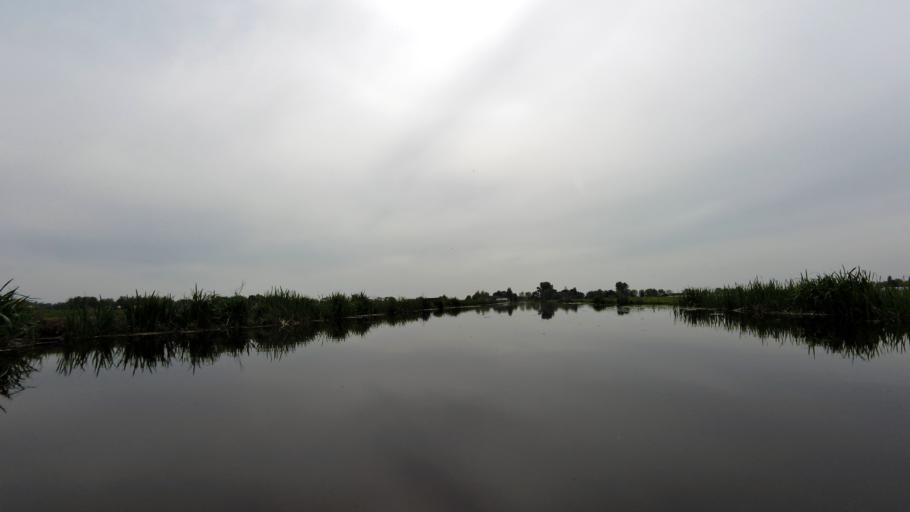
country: NL
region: South Holland
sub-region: Bodegraven-Reeuwijk
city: Reeuwijk
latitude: 52.0641
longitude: 4.7184
